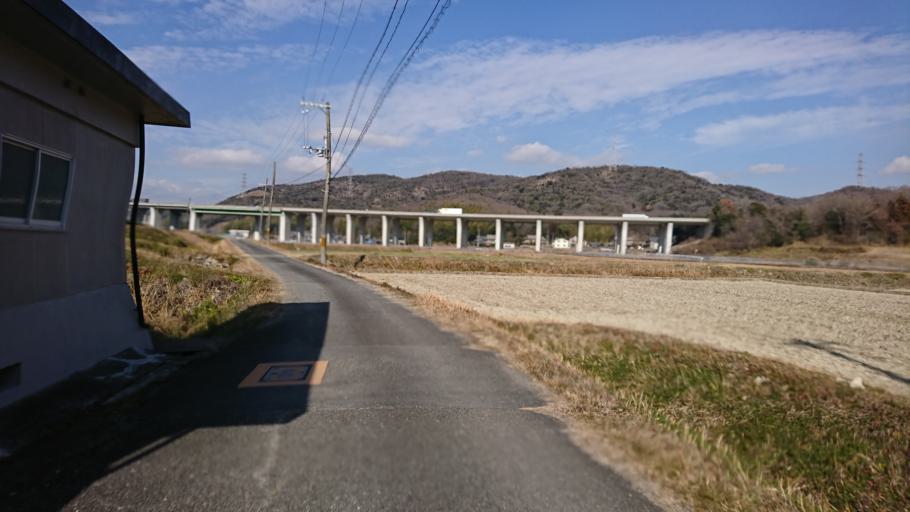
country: JP
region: Hyogo
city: Ono
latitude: 34.8364
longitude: 134.8652
